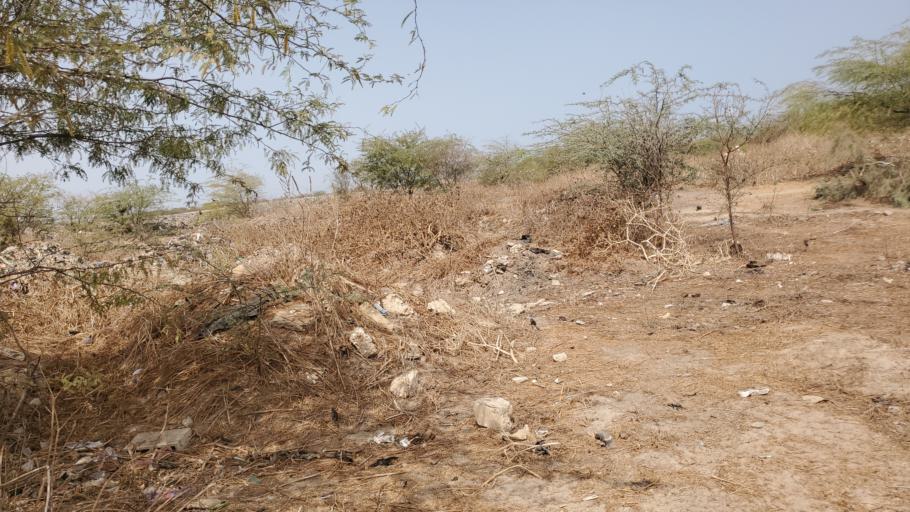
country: SN
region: Saint-Louis
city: Saint-Louis
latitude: 15.9500
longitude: -16.4305
